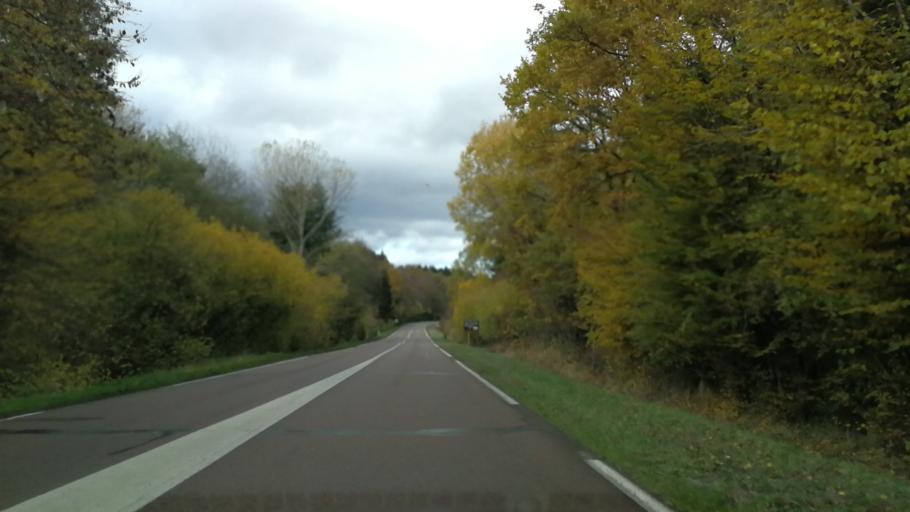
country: FR
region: Bourgogne
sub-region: Departement de la Cote-d'Or
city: Saulieu
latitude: 47.2548
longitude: 4.2737
